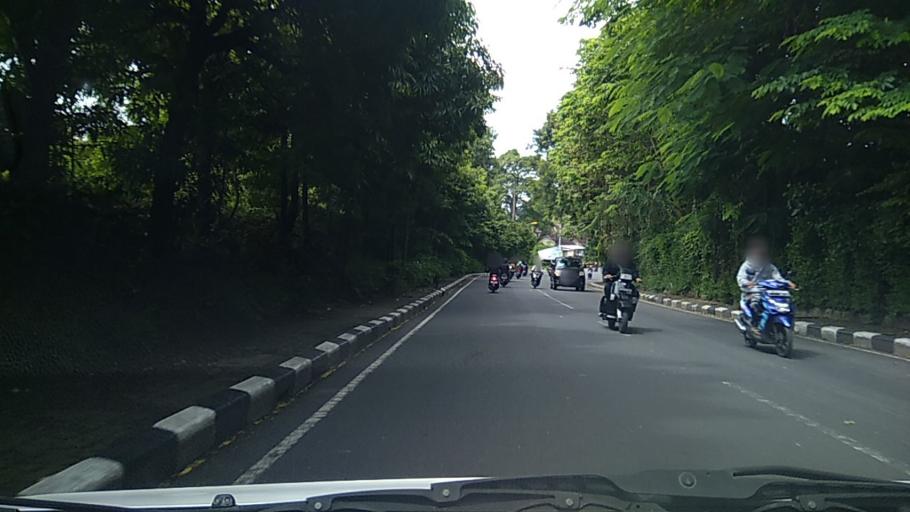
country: ID
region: Bali
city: Dajan Tangluk
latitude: -8.6445
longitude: 115.2480
